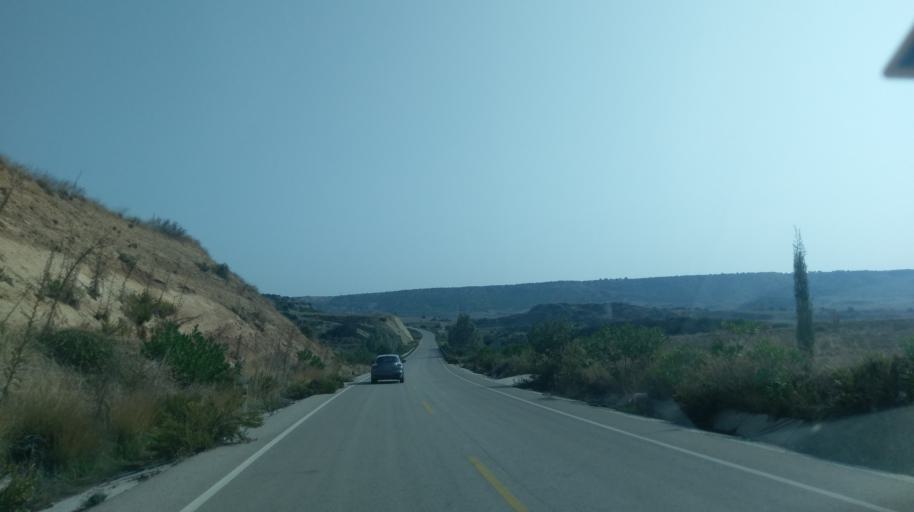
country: CY
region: Ammochostos
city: Leonarisso
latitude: 35.4799
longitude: 34.1117
